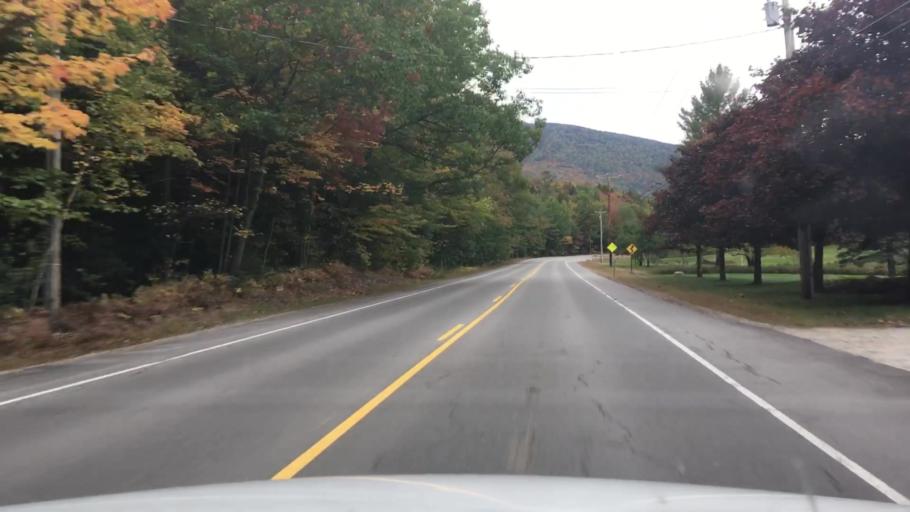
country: US
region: New Hampshire
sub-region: Coos County
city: Gorham
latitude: 44.3676
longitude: -71.1749
